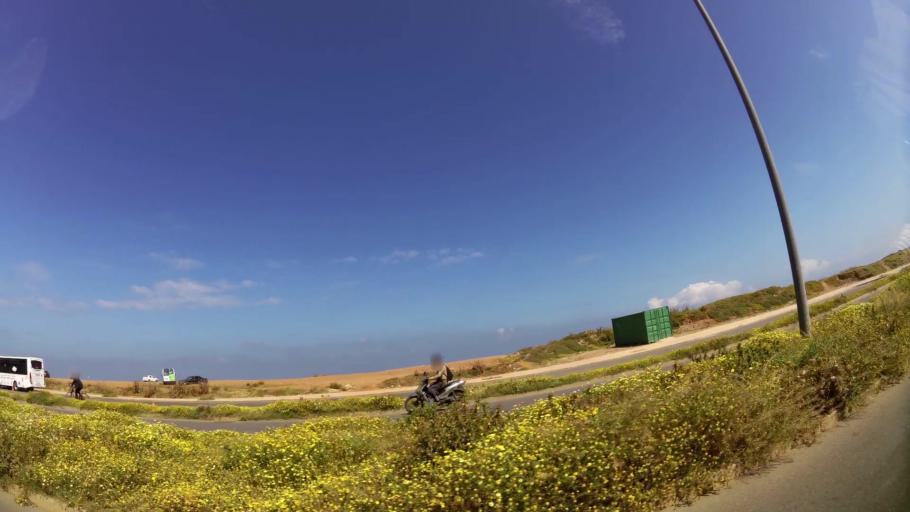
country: MA
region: Rabat-Sale-Zemmour-Zaer
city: Sale
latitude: 34.0747
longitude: -6.7985
